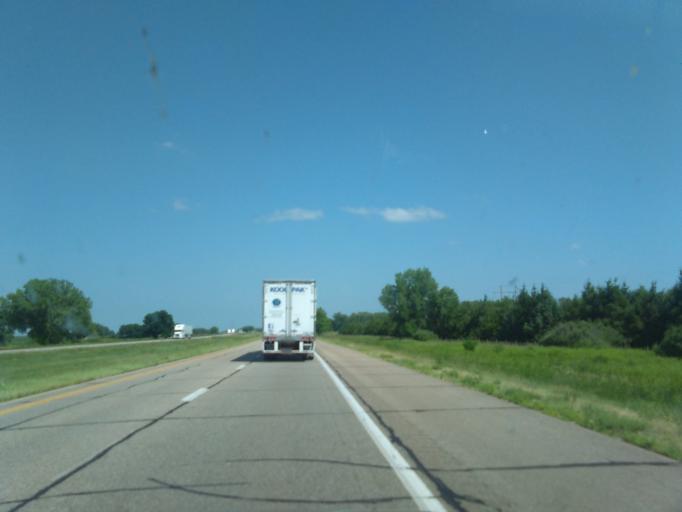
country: US
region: Nebraska
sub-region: Buffalo County
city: Kearney
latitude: 40.6853
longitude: -99.3198
